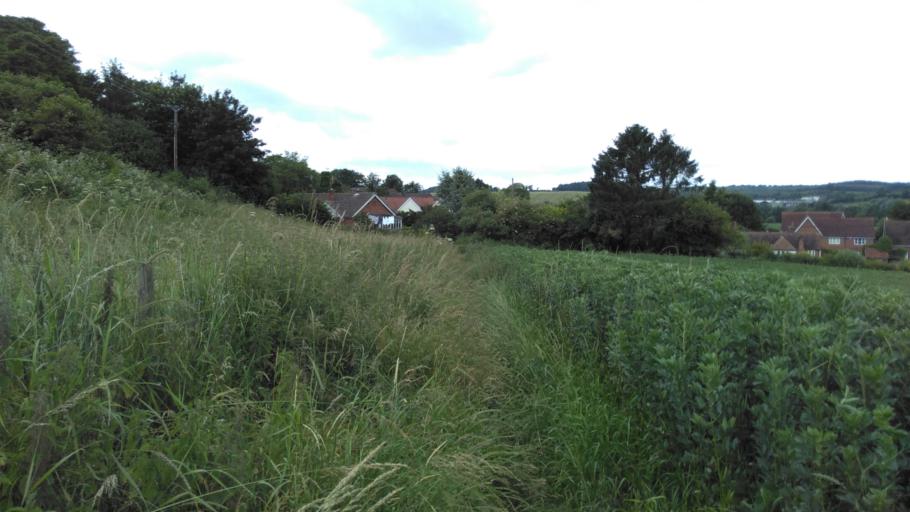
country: GB
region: England
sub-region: Kent
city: Chartham
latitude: 51.2533
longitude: 1.0102
